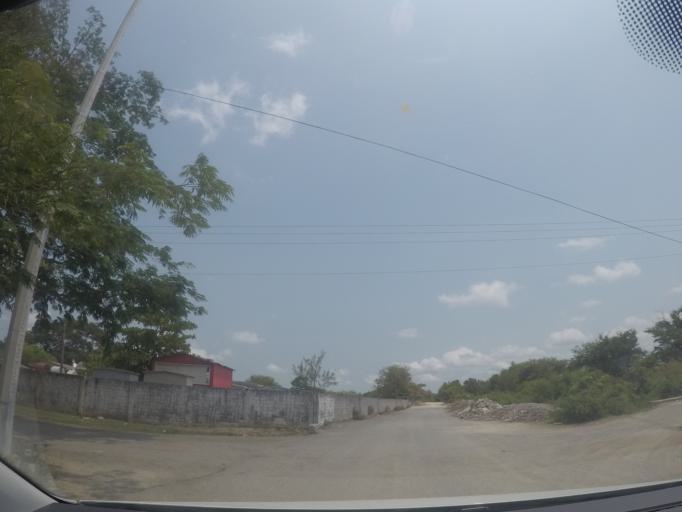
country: MX
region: Oaxaca
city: Asuncion Ixtaltepec
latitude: 16.5049
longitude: -95.0662
